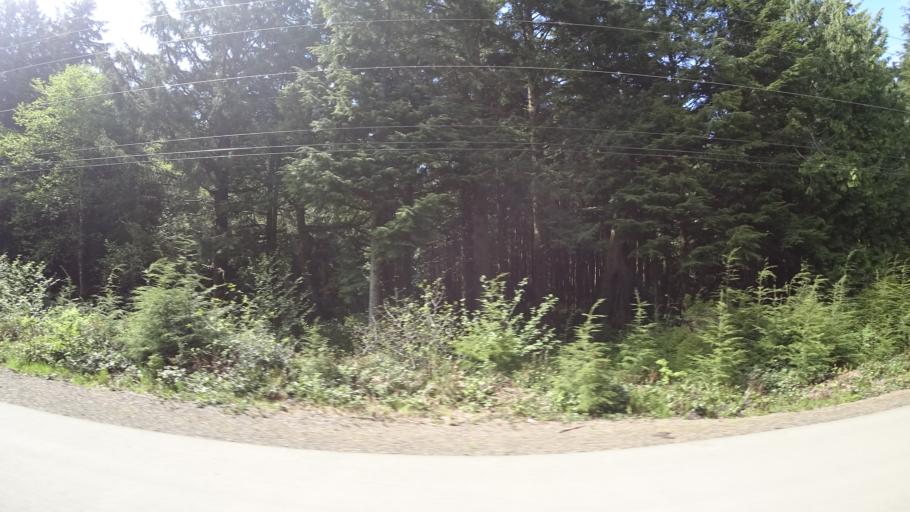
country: US
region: Oregon
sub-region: Lincoln County
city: Lincoln Beach
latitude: 44.8343
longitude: -124.0545
